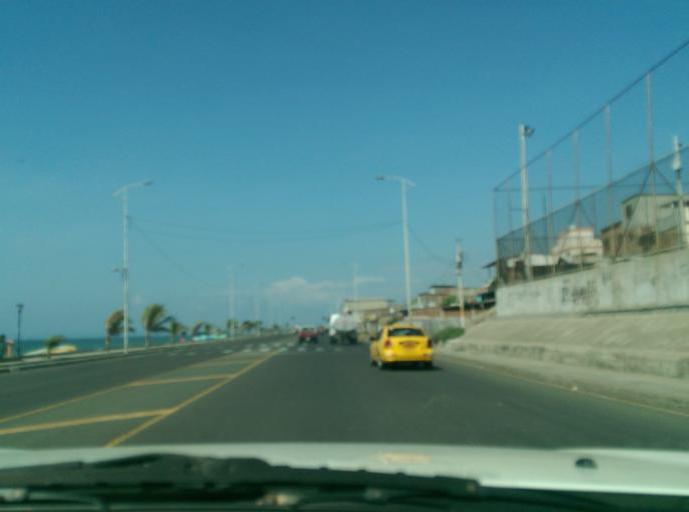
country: EC
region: Manabi
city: Manta
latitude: -0.9500
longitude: -80.7052
